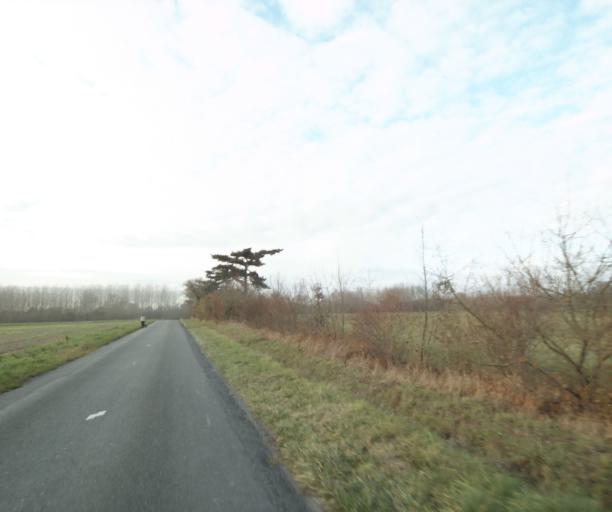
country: FR
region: Poitou-Charentes
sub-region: Departement de la Charente-Maritime
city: Les Gonds
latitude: 45.7074
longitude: -0.5981
